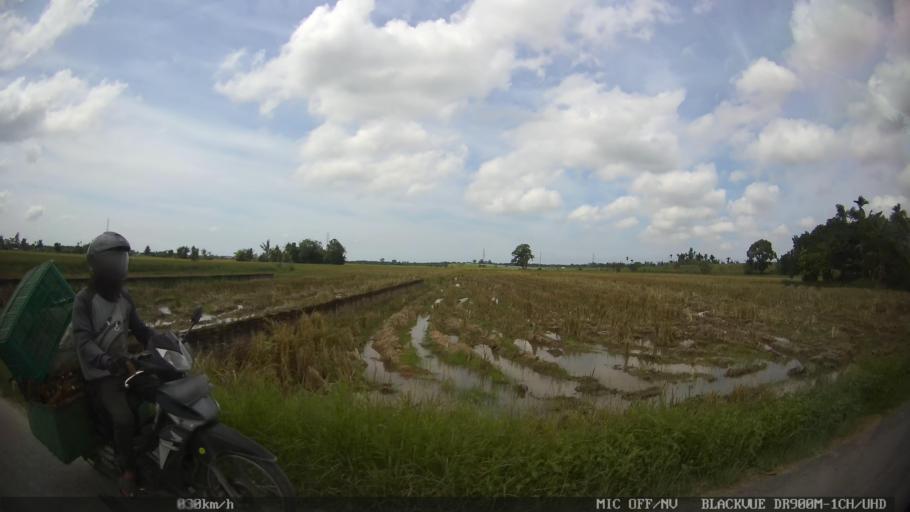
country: ID
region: North Sumatra
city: Percut
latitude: 3.5710
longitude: 98.8459
